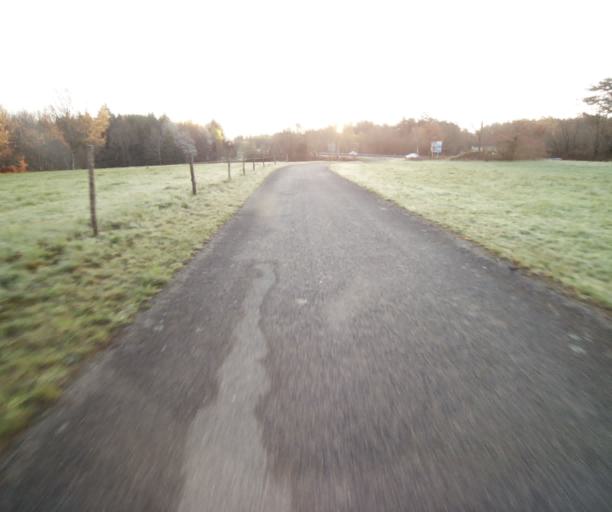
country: FR
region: Limousin
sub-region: Departement de la Correze
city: Correze
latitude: 45.3205
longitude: 1.8455
